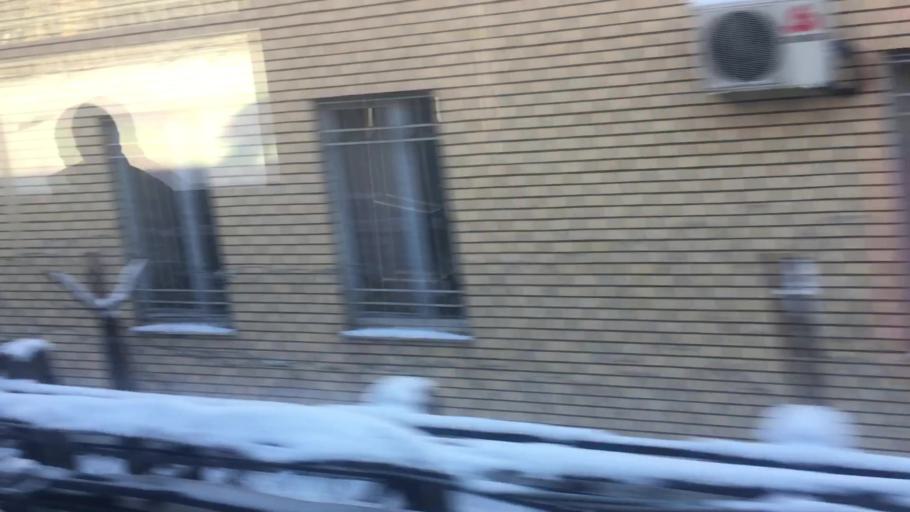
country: RU
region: Moskovskaya
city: Fili
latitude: 55.7451
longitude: 37.5022
